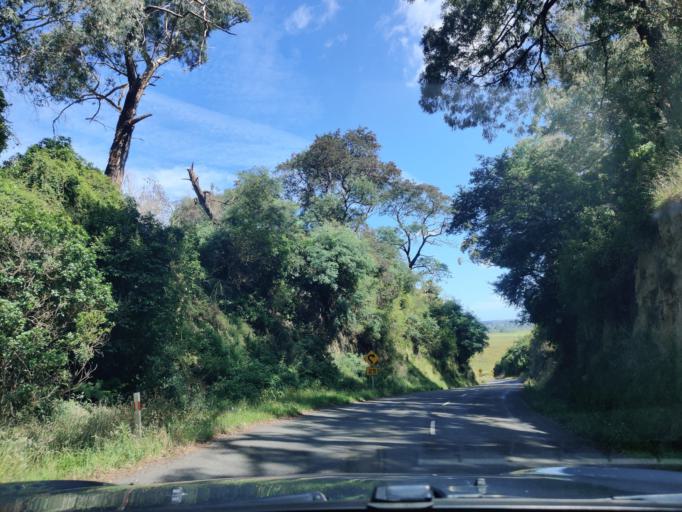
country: NZ
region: Manawatu-Wanganui
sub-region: Rangitikei District
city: Bulls
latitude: -40.1726
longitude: 175.4336
